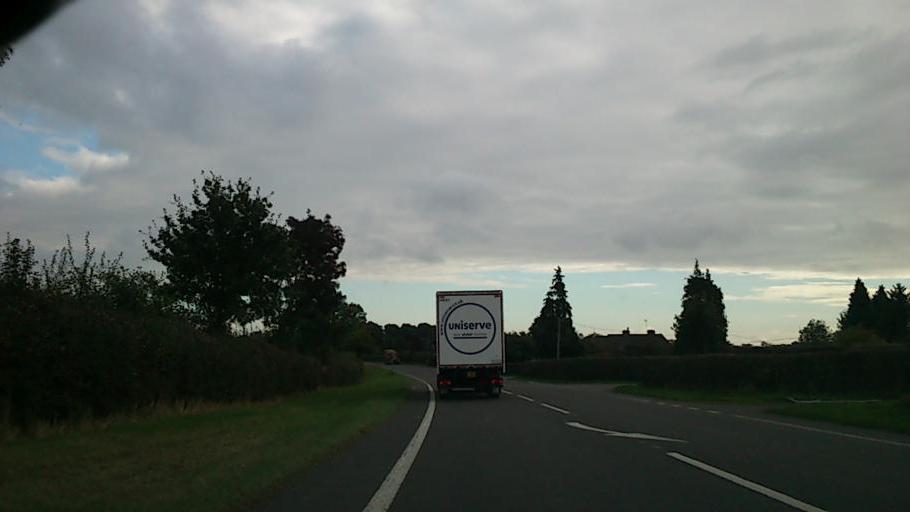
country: GB
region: England
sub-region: Shropshire
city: Westbury
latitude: 52.7062
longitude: -2.9035
